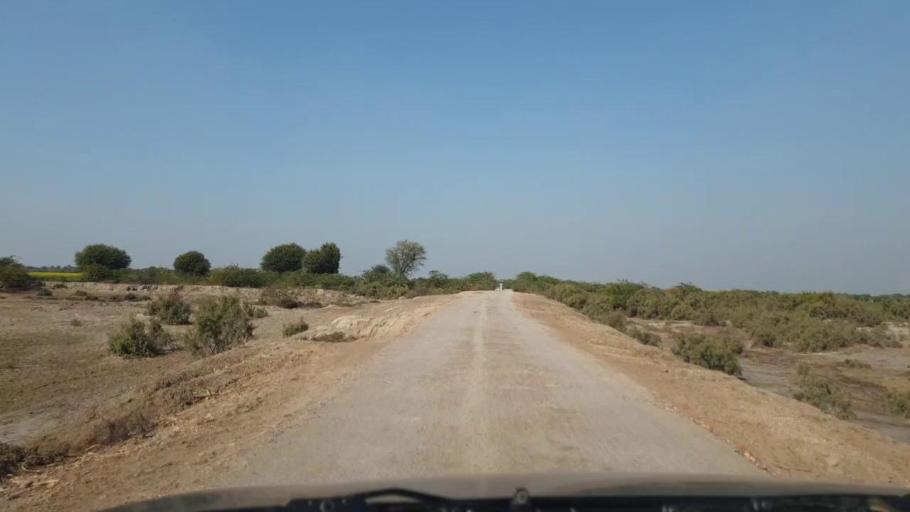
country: PK
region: Sindh
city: Jhol
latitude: 25.9047
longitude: 68.8312
